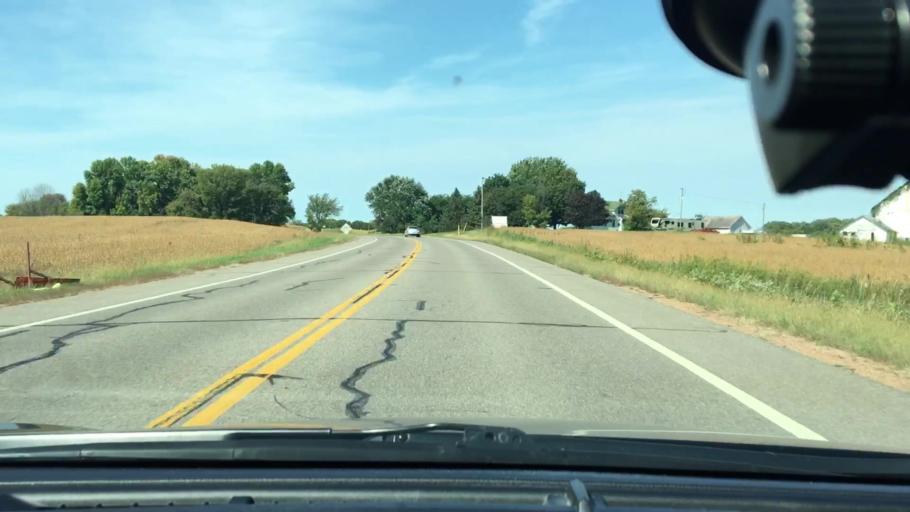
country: US
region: Minnesota
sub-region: Hennepin County
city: Corcoran
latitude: 45.0905
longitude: -93.5353
